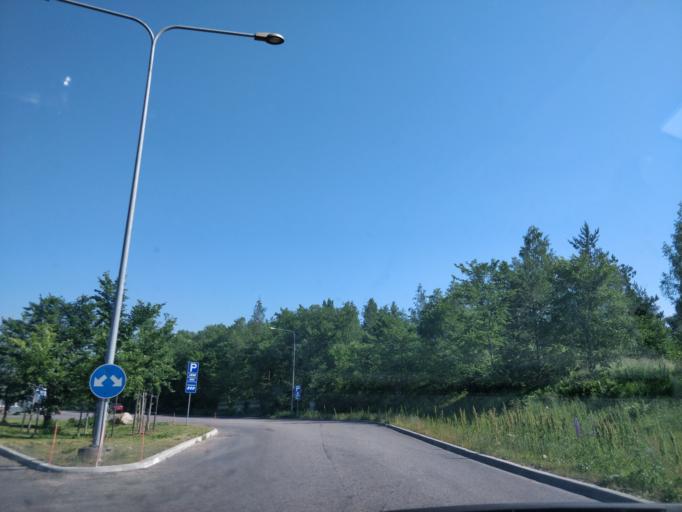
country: FI
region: Uusimaa
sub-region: Helsinki
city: Nurmijaervi
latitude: 60.5061
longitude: 24.8512
